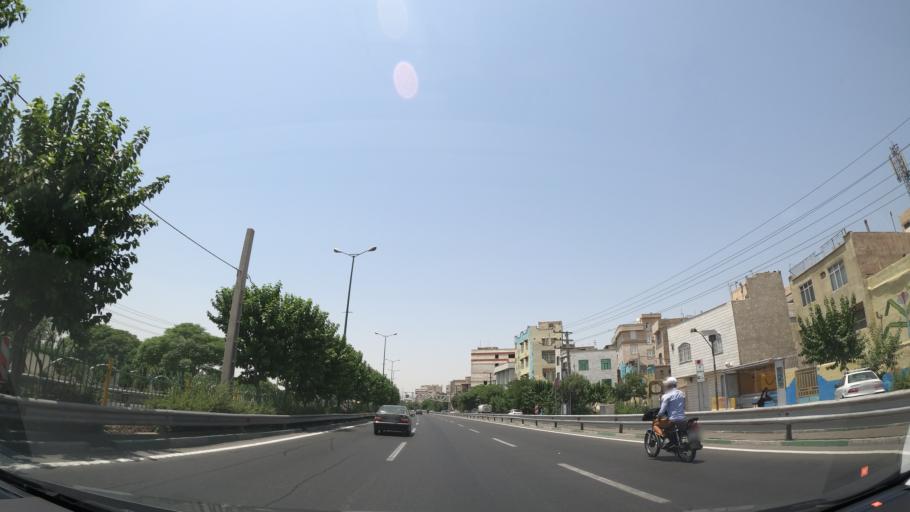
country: IR
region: Tehran
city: Tehran
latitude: 35.6509
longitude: 51.3877
